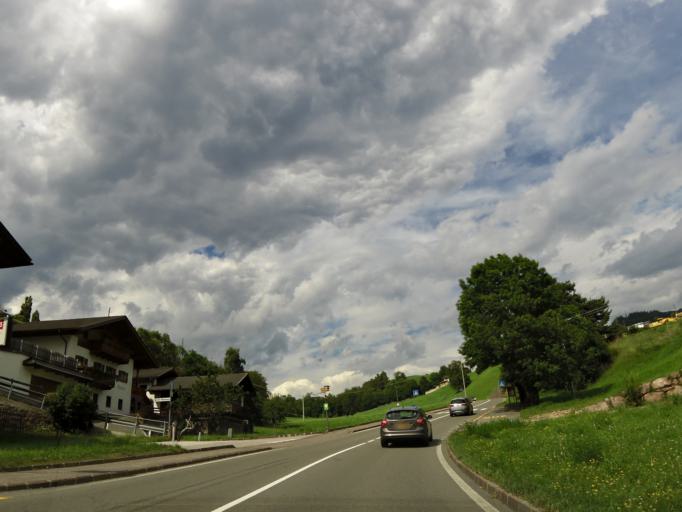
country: IT
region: Trentino-Alto Adige
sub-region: Bolzano
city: Siusi
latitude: 46.5507
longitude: 11.5550
